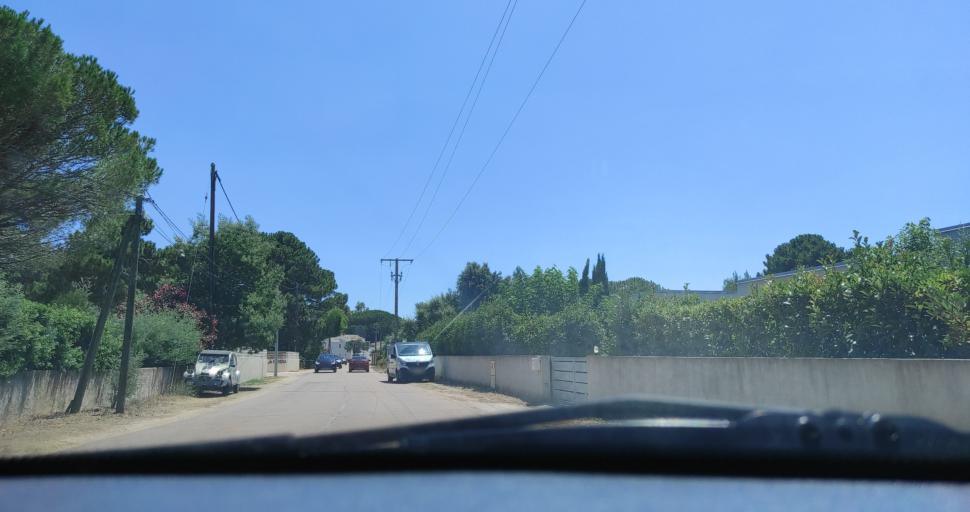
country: FR
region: Corsica
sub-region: Departement de la Corse-du-Sud
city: Porto-Vecchio
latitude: 41.6306
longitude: 9.3326
